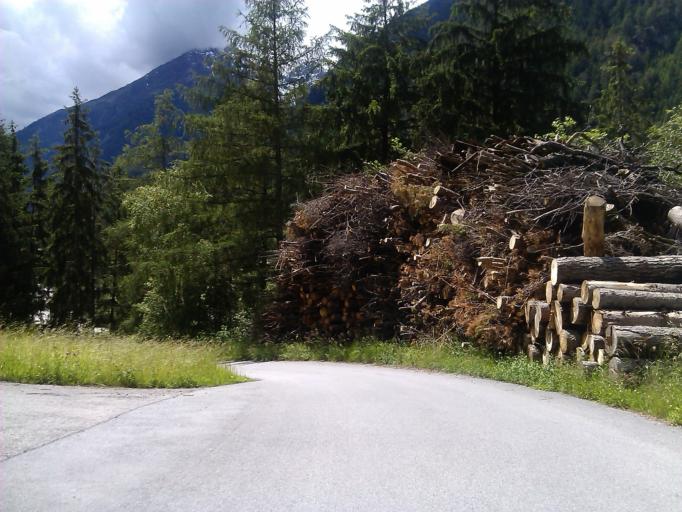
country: AT
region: Tyrol
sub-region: Politischer Bezirk Landeck
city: Pfunds
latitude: 46.9544
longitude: 10.5155
